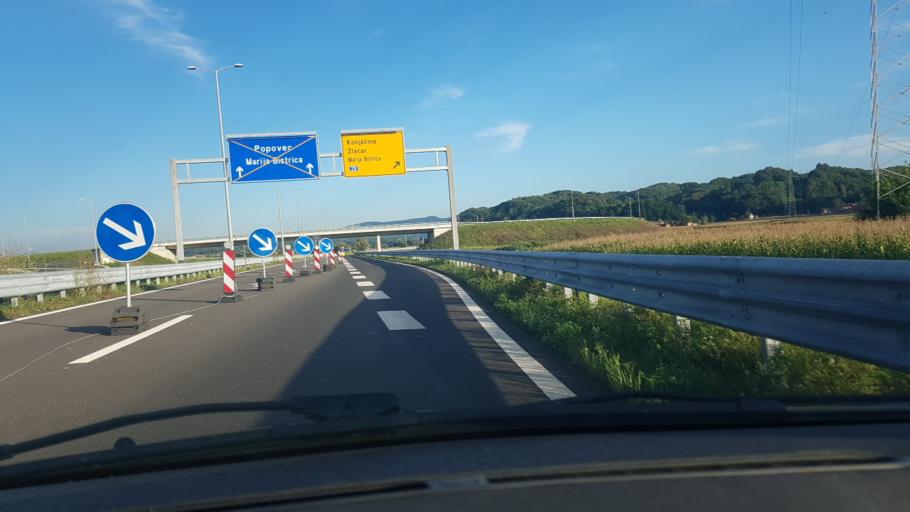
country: HR
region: Krapinsko-Zagorska
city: Selnica
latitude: 46.0385
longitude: 16.0726
